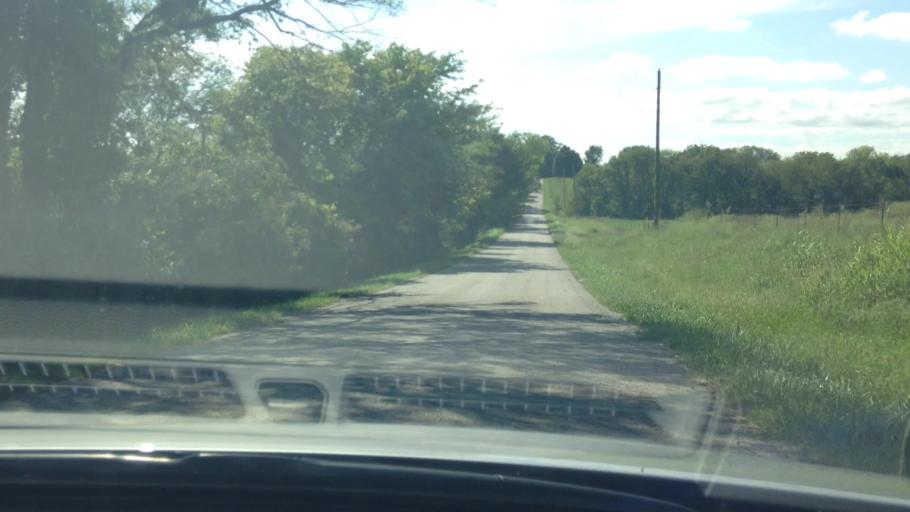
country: US
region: Missouri
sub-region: Clay County
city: Smithville
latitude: 39.3402
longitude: -94.6625
